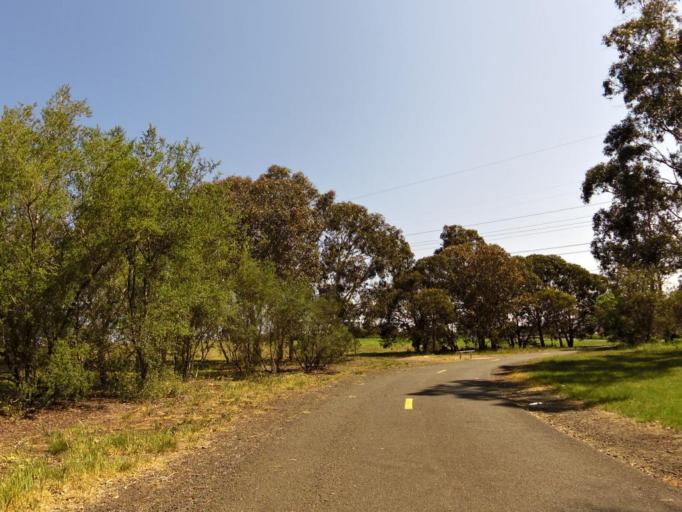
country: AU
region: Victoria
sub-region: Moreland
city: Glenroy
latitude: -37.6945
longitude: 144.9380
